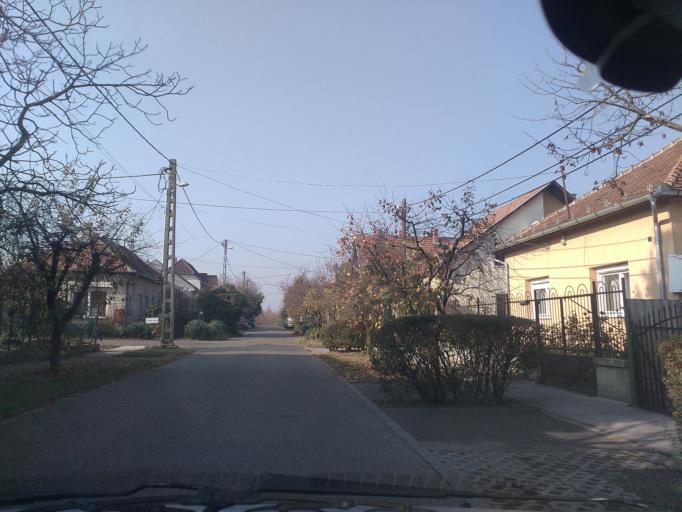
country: HU
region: Budapest
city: Budapest XVIII. keruelet
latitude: 47.4412
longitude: 19.1972
